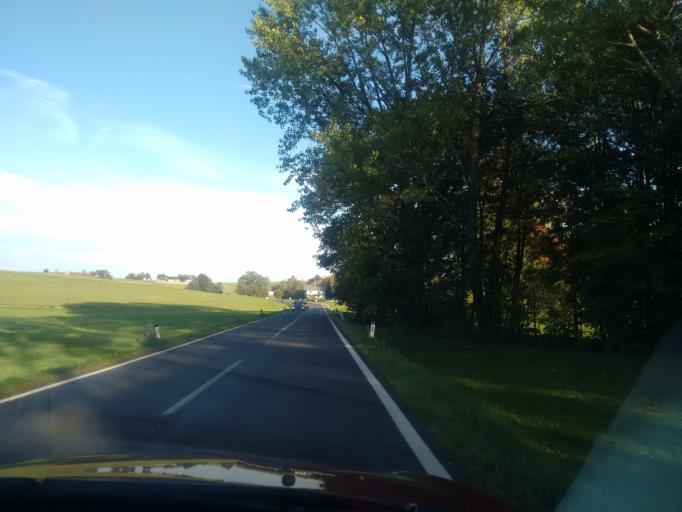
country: AT
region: Upper Austria
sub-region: Politischer Bezirk Vocklabruck
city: Manning
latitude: 48.0849
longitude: 13.6493
